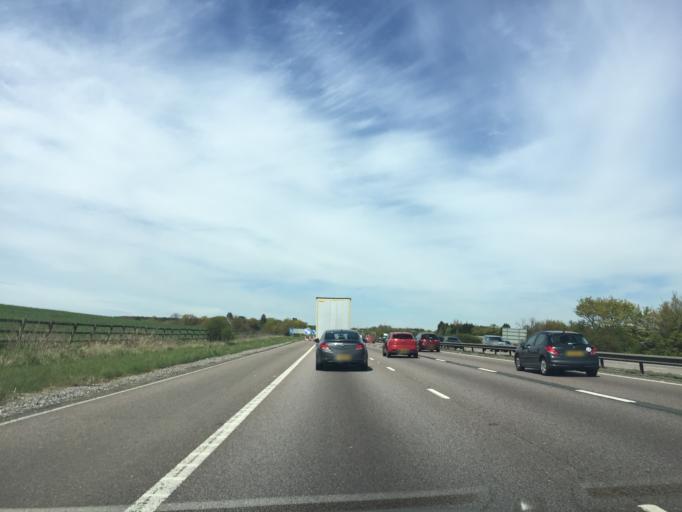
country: GB
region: England
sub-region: Essex
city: Epping
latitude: 51.7335
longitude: 0.1380
